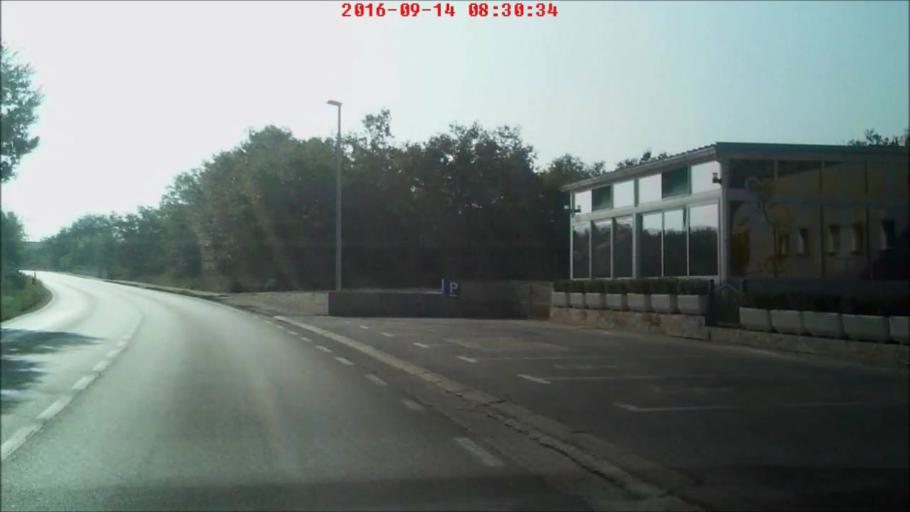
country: HR
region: Zadarska
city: Zadar
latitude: 44.1718
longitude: 15.2900
